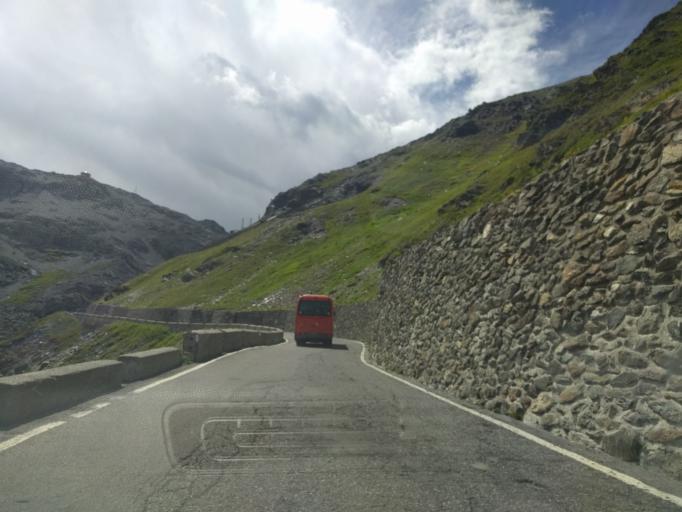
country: IT
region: Lombardy
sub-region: Provincia di Sondrio
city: Sant'Antonio
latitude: 46.5327
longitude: 10.4599
